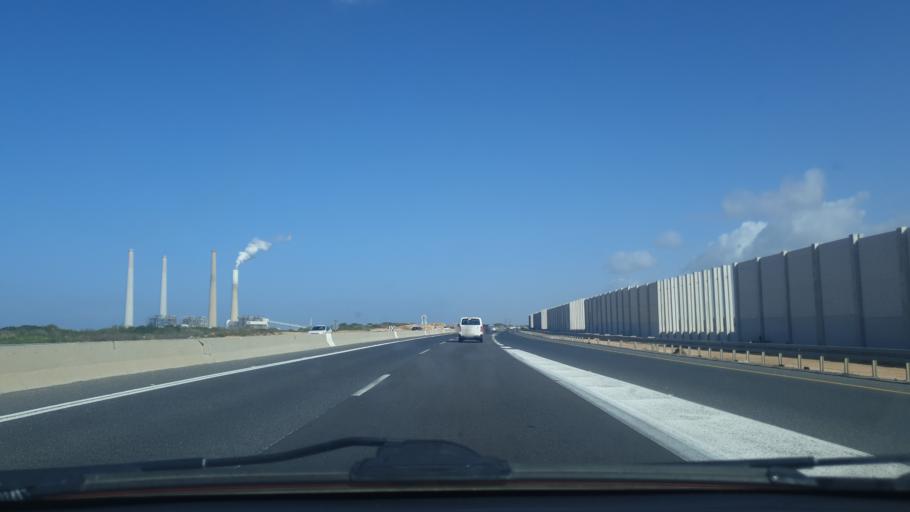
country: IL
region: Haifa
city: Hadera
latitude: 32.4502
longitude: 34.8927
